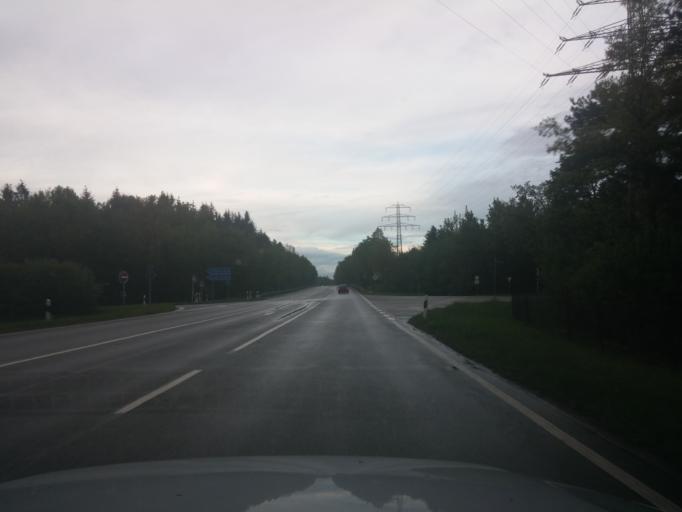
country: DE
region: Bavaria
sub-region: Upper Bavaria
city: Hohenbrunn
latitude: 48.0596
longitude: 11.7077
